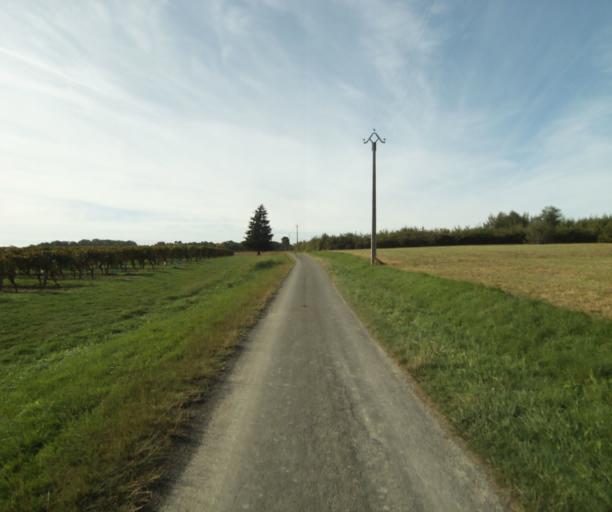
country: FR
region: Midi-Pyrenees
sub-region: Departement du Gers
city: Eauze
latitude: 43.9236
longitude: 0.1250
